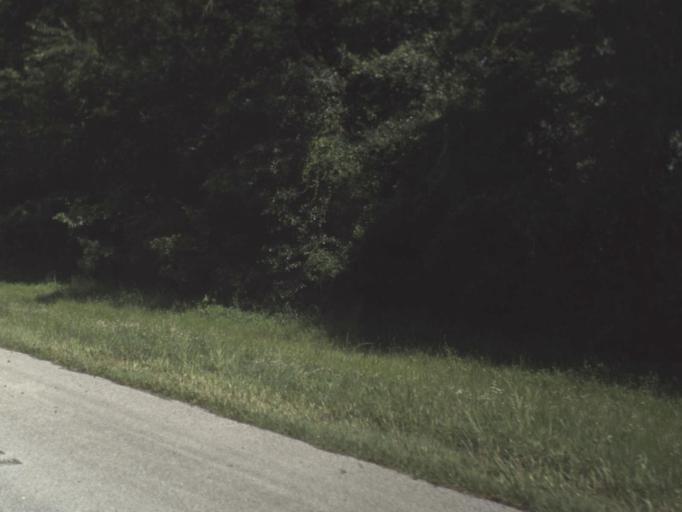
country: US
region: Florida
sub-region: Duval County
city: Baldwin
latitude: 30.2841
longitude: -82.0339
